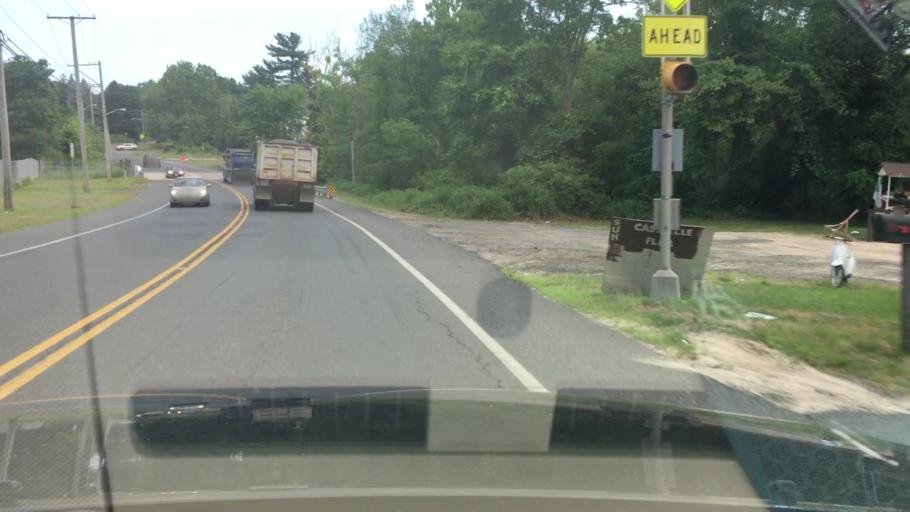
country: US
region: New Jersey
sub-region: Ocean County
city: Vista Center
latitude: 40.1099
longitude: -74.3882
